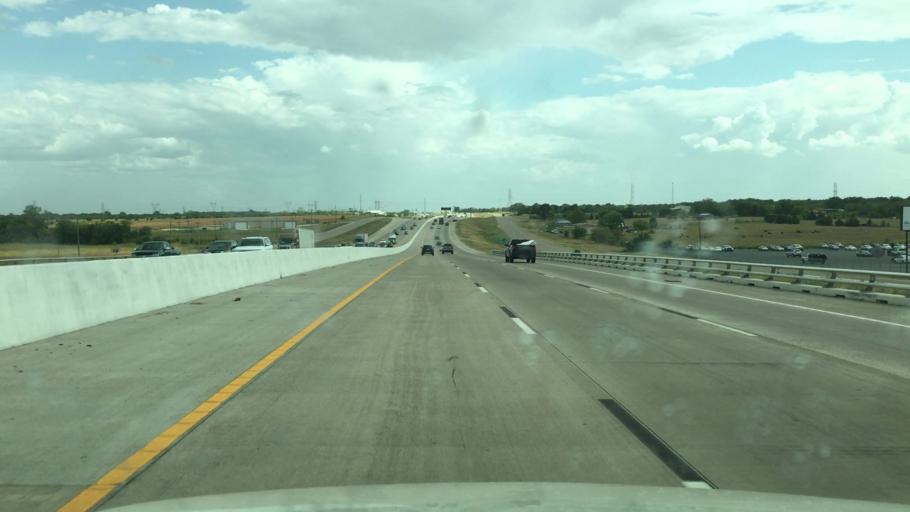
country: US
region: Texas
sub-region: McLennan County
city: Northcrest
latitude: 31.7141
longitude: -97.1024
